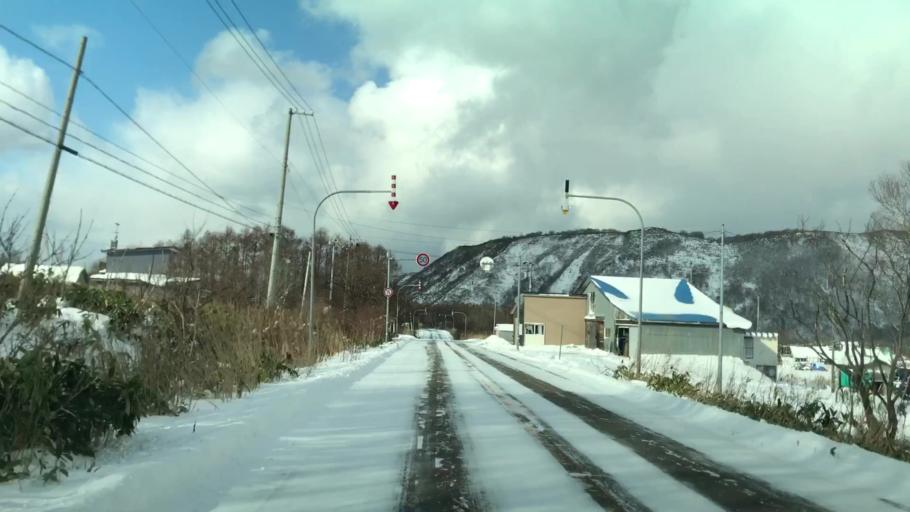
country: JP
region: Hokkaido
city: Yoichi
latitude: 43.3278
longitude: 140.4962
